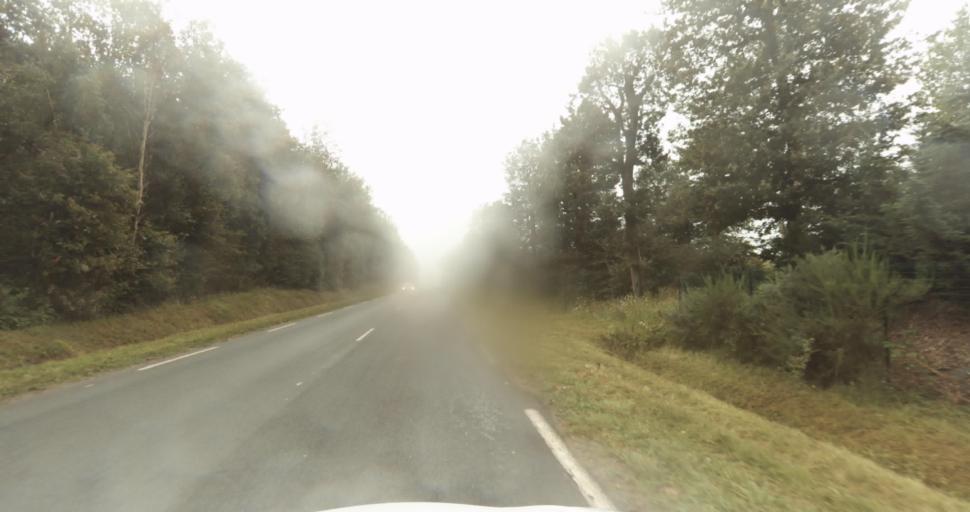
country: FR
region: Haute-Normandie
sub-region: Departement de l'Eure
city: Normanville
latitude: 49.0941
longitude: 1.1757
